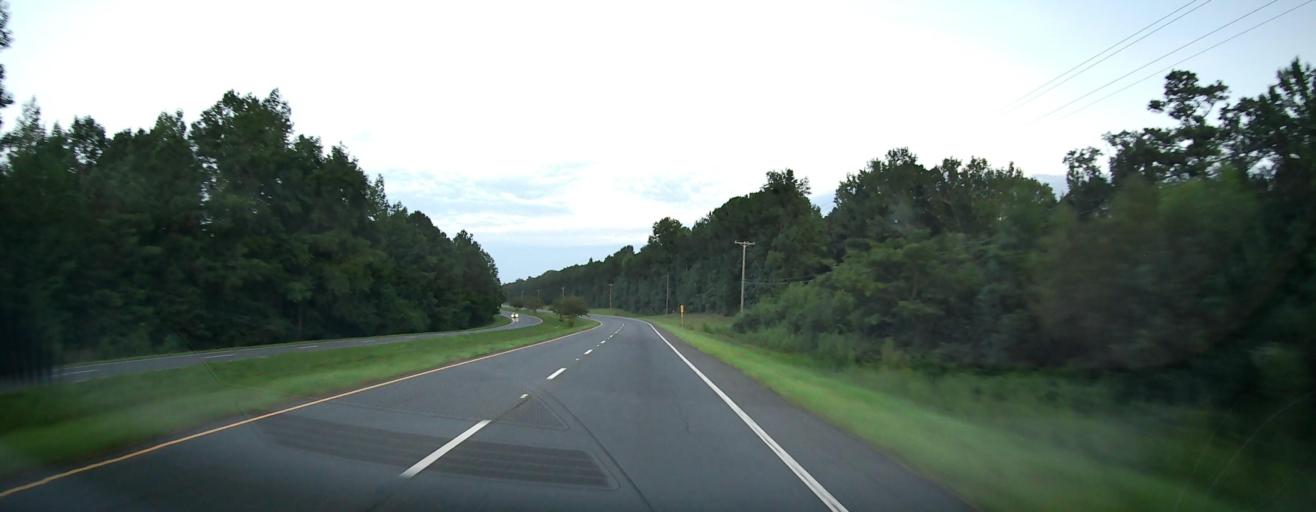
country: US
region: Georgia
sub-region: Muscogee County
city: Columbus
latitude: 32.5502
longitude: -84.7954
